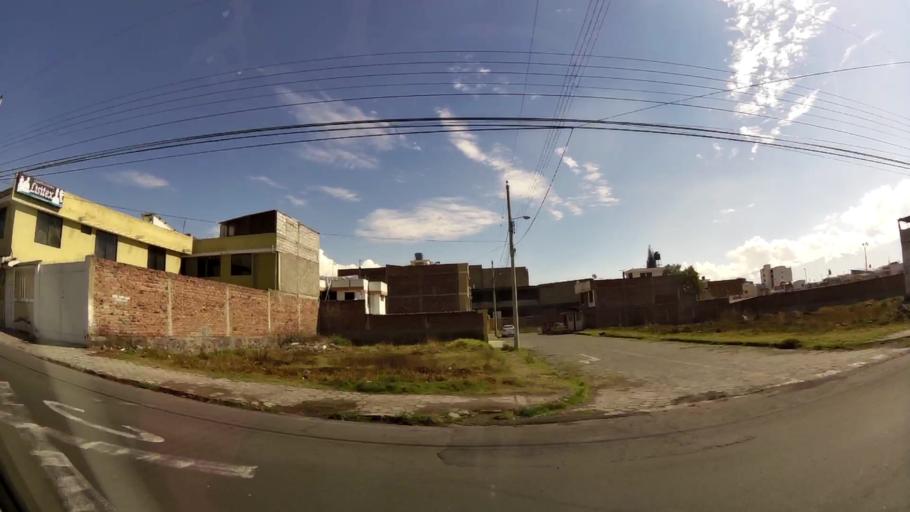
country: EC
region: Chimborazo
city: Riobamba
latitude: -1.6630
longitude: -78.6668
